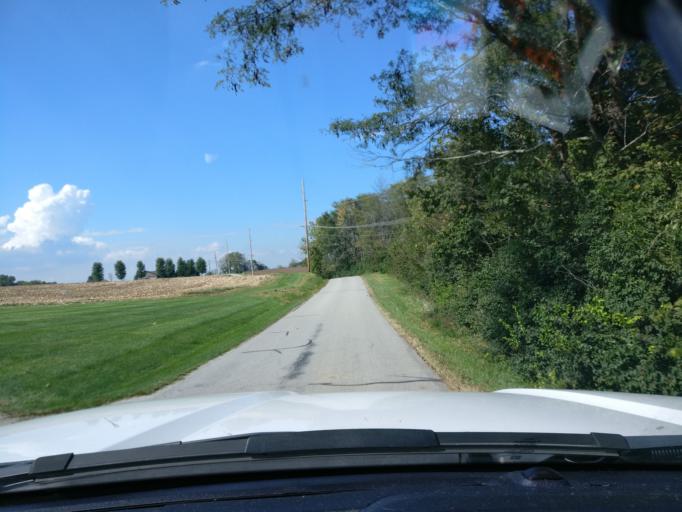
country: US
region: Ohio
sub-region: Clinton County
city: Wilmington
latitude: 39.4627
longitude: -83.9568
